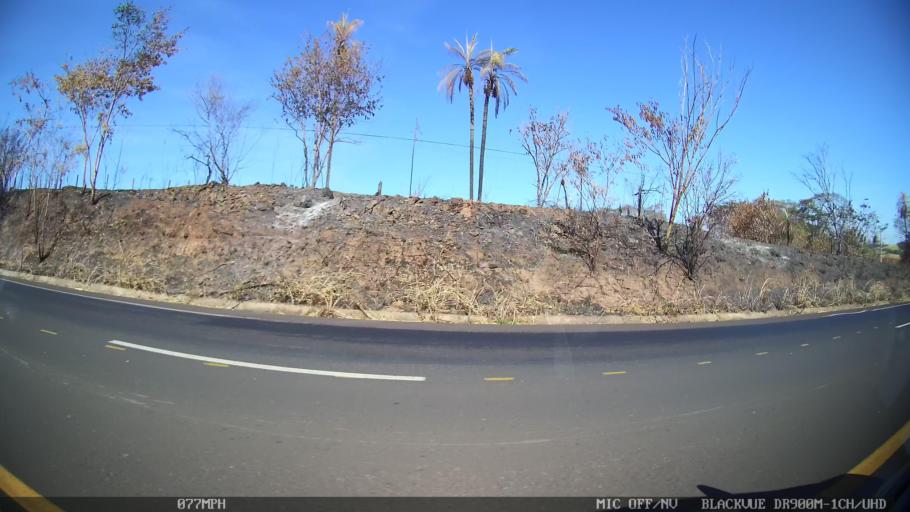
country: BR
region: Sao Paulo
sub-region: Barretos
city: Barretos
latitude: -20.6122
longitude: -48.7544
